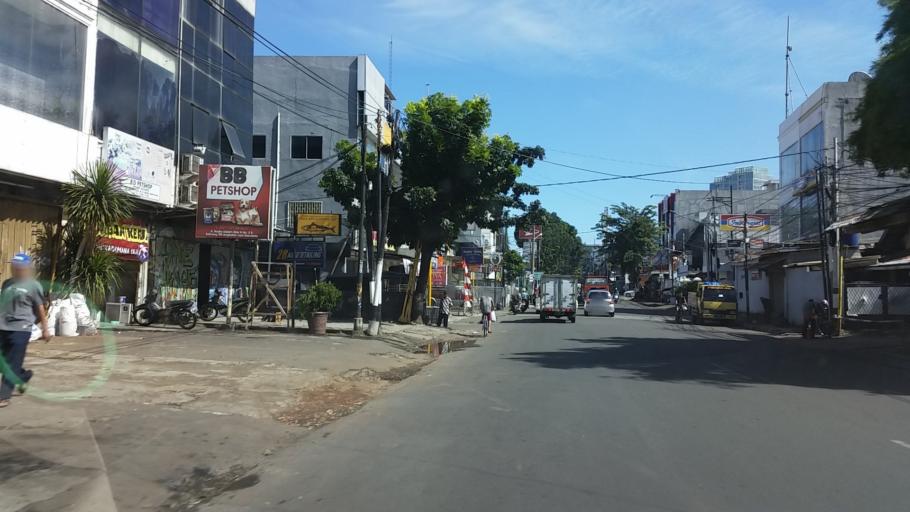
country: ID
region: Jakarta Raya
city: Jakarta
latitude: -6.2529
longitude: 106.7911
